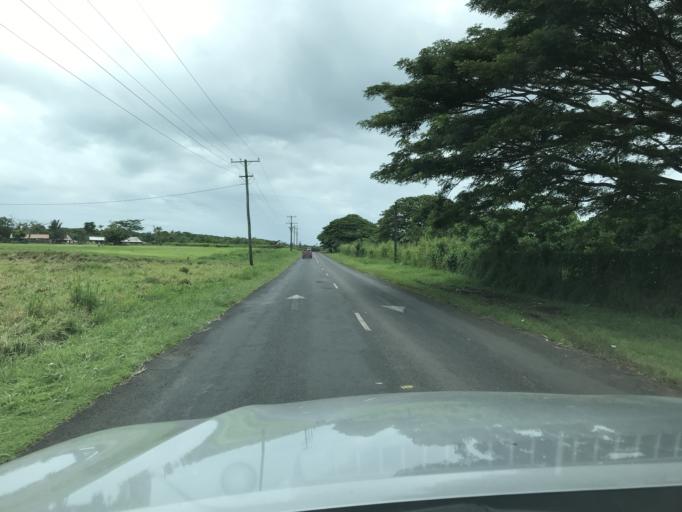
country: WS
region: Aiga-i-le-Tai
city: Mulifanua
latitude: -13.8331
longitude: -172.0234
